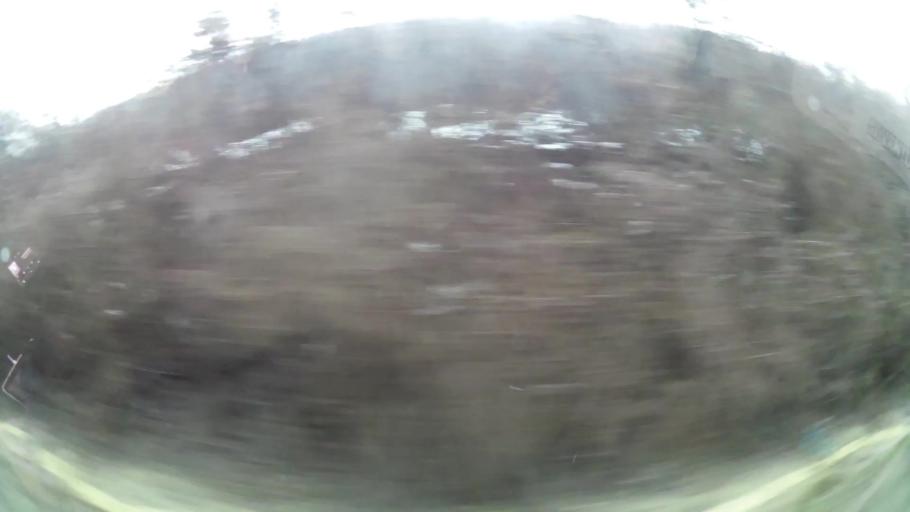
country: XK
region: Ferizaj
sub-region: Hani i Elezit
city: Hani i Elezit
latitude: 42.1640
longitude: 21.2770
